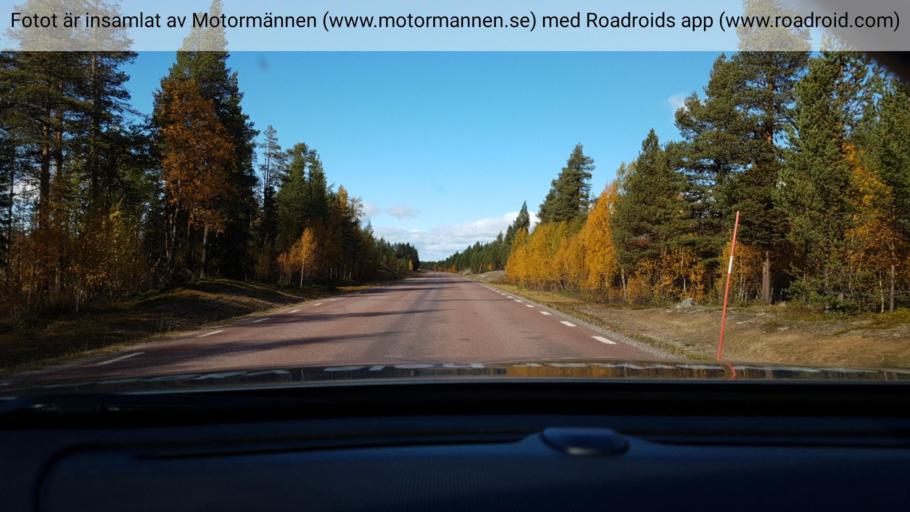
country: SE
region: Norrbotten
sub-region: Arjeplogs Kommun
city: Arjeplog
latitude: 65.9928
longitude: 18.1760
